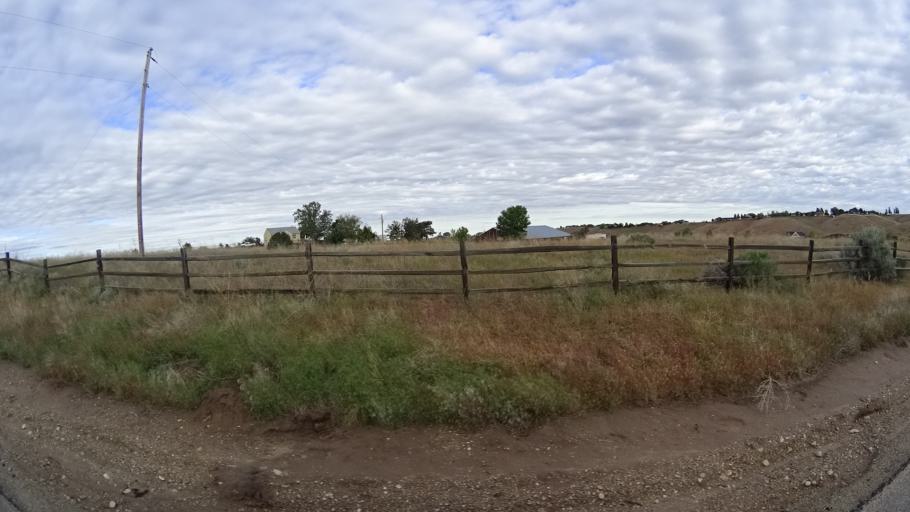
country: US
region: Idaho
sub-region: Ada County
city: Star
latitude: 43.7346
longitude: -116.5128
